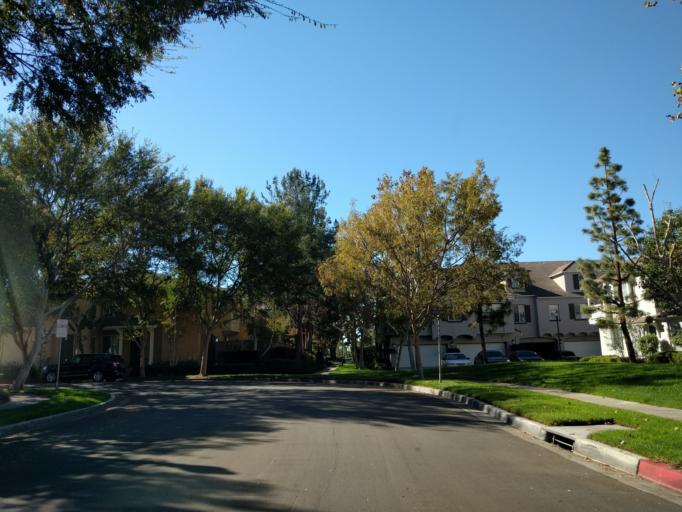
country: US
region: California
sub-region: Orange County
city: North Tustin
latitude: 33.7180
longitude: -117.7776
